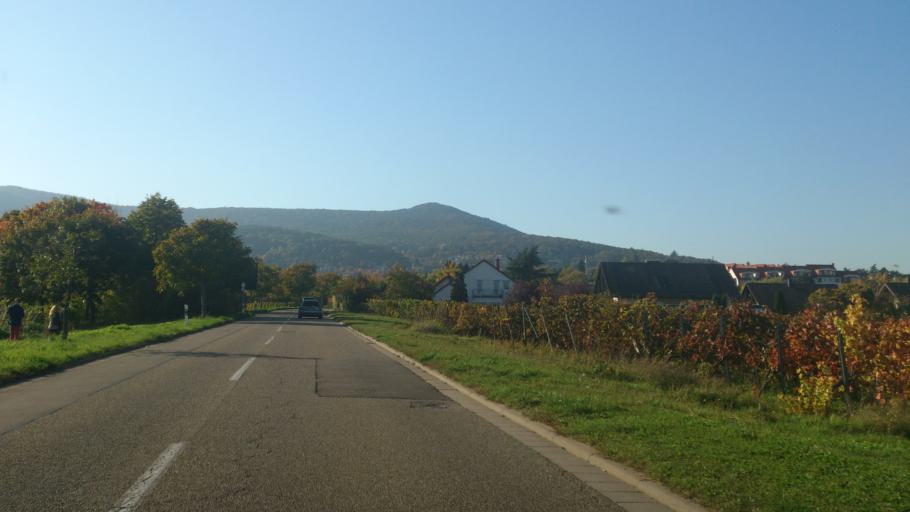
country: DE
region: Rheinland-Pfalz
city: Neustadt
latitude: 49.3399
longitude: 8.1479
